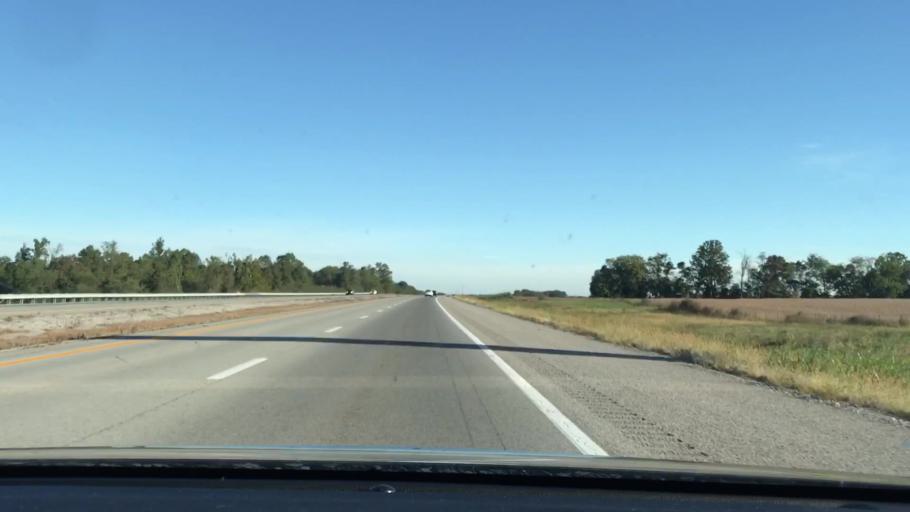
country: US
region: Kentucky
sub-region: Christian County
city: Hopkinsville
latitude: 36.7765
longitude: -87.4981
